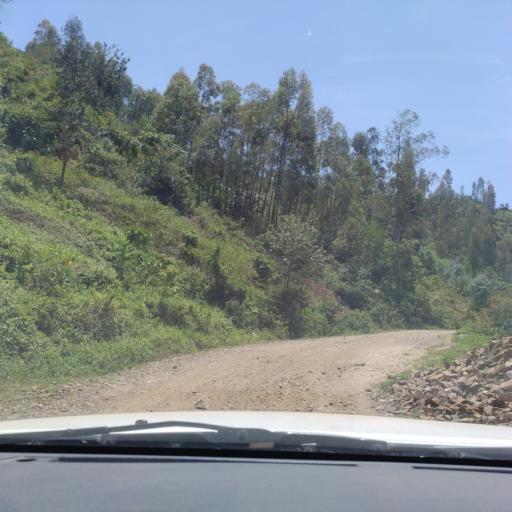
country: CD
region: Nord Kivu
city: Sake
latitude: -1.9645
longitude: 28.9137
